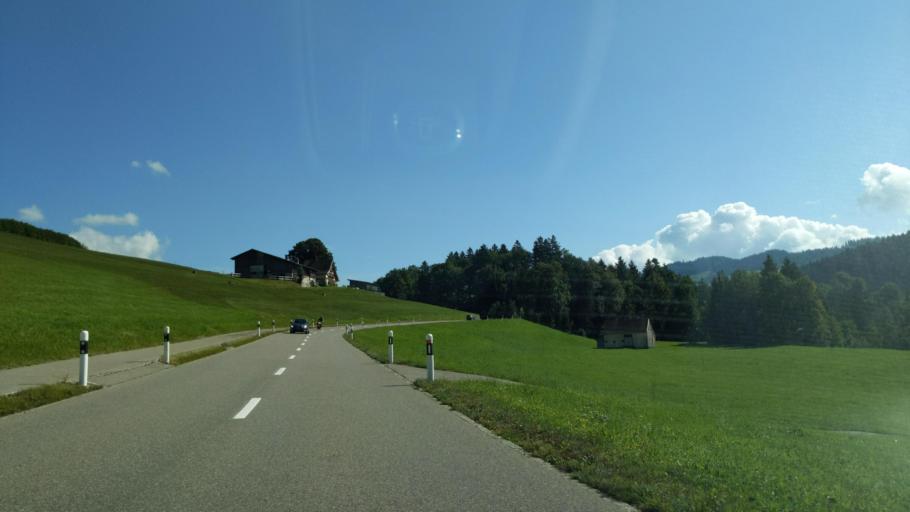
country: CH
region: Saint Gallen
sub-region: Wahlkreis Toggenburg
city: Sankt Peterzell
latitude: 47.3185
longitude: 9.1875
